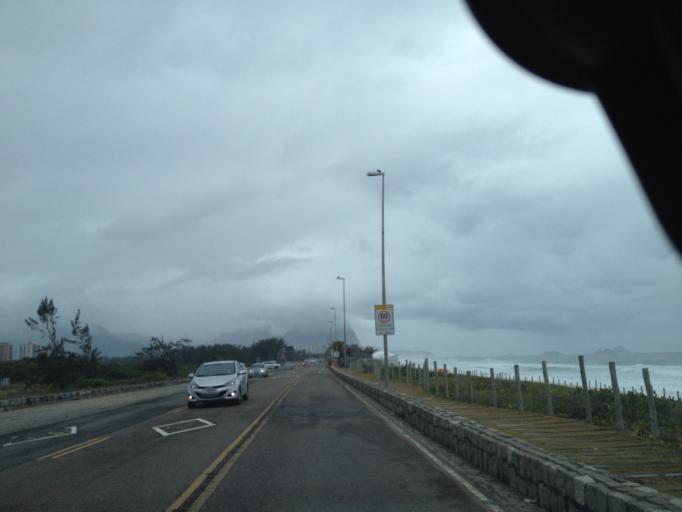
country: BR
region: Rio de Janeiro
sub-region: Nilopolis
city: Nilopolis
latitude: -23.0138
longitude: -43.3993
